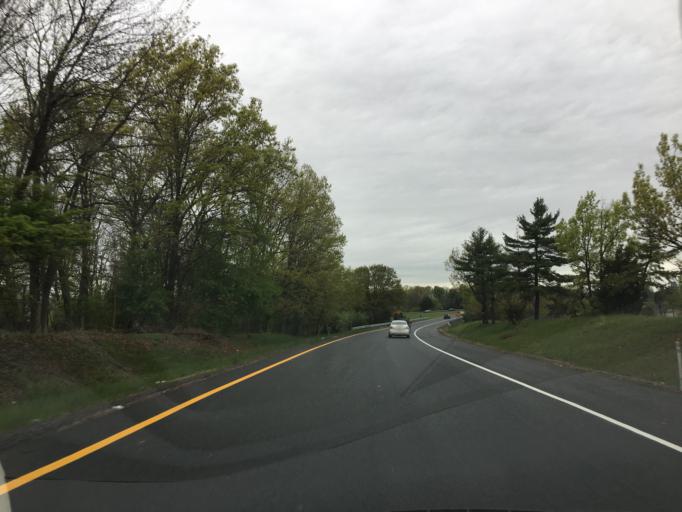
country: US
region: Maryland
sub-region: Baltimore County
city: Woodlawn
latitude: 39.3074
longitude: -76.7407
